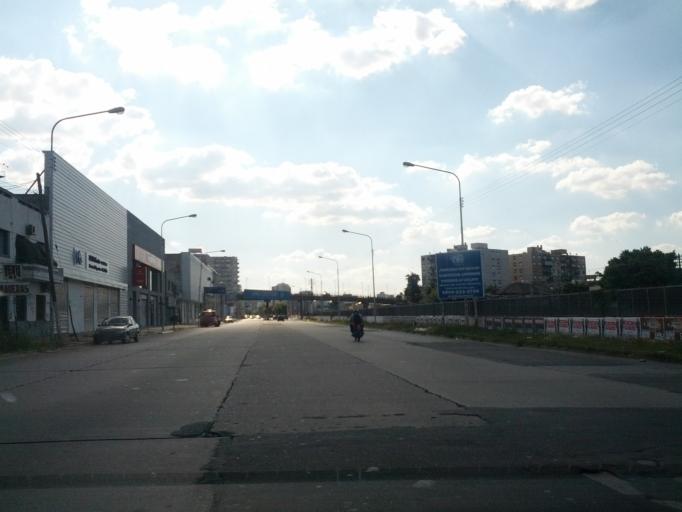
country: AR
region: Buenos Aires
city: San Justo
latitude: -34.6402
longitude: -58.5465
